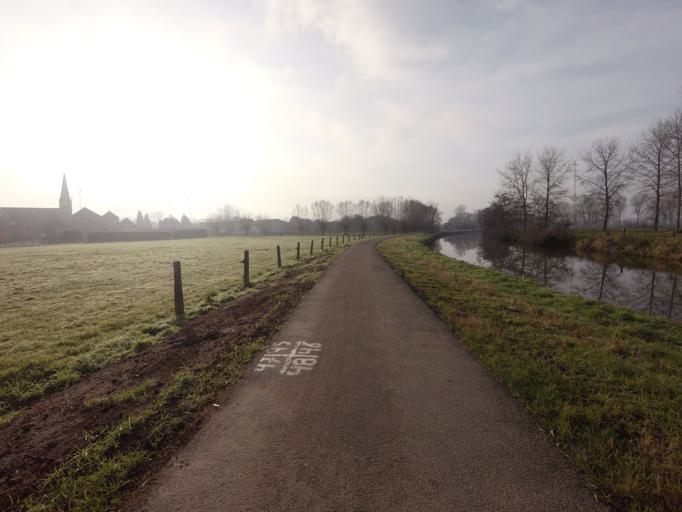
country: BE
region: Flanders
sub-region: Provincie Vlaams-Brabant
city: Galmaarden
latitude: 50.7970
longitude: 3.9508
